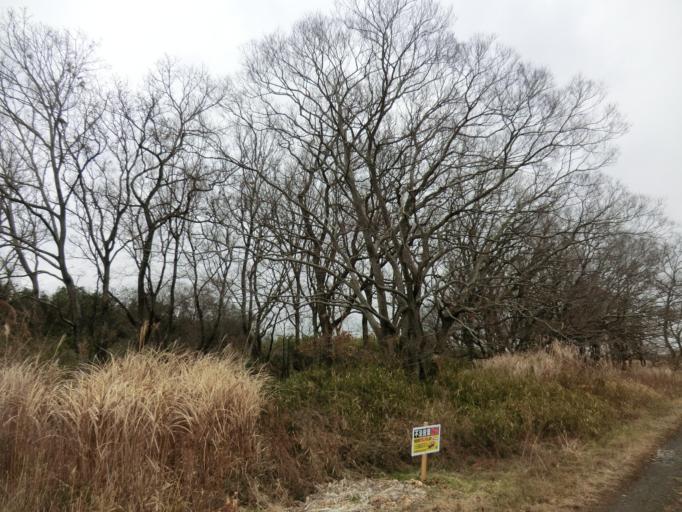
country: JP
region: Ibaraki
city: Naka
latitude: 36.1168
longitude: 140.1333
